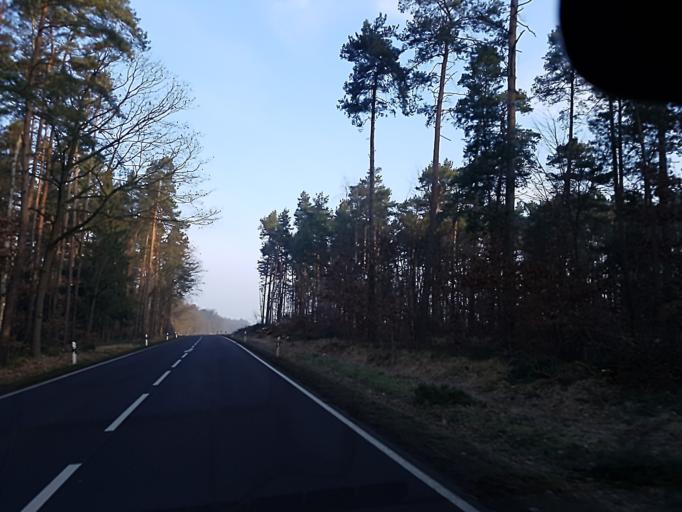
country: DE
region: Brandenburg
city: Wiesenburg
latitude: 52.0628
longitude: 12.4518
